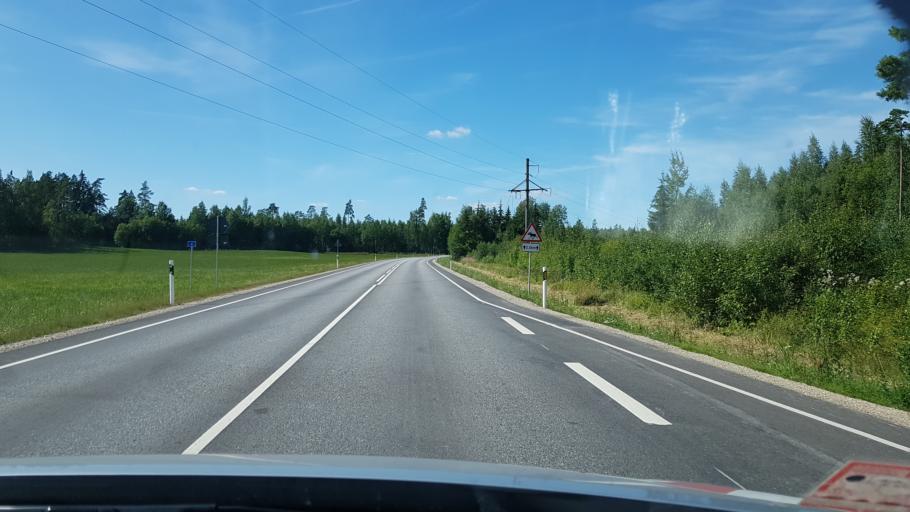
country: EE
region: Polvamaa
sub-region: Polva linn
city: Polva
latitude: 58.0371
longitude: 27.1327
